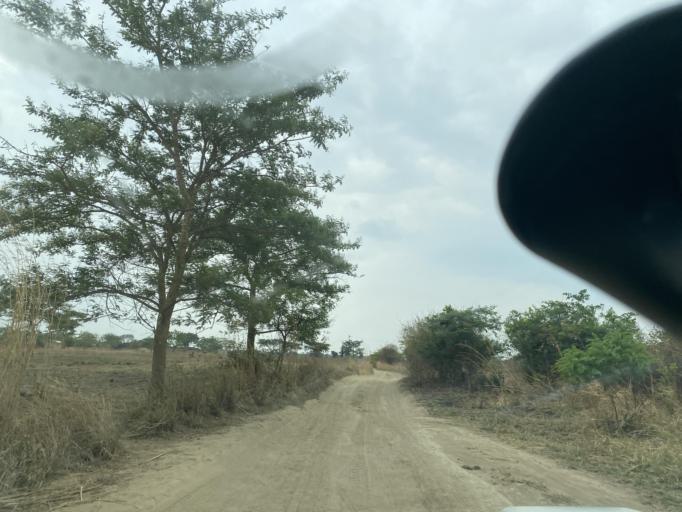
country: ZM
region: Lusaka
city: Lusaka
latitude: -15.2411
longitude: 28.3334
